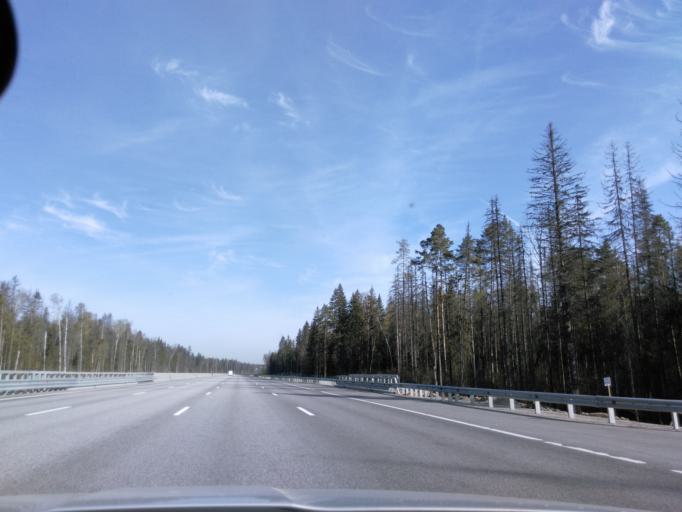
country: RU
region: Moskovskaya
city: Rzhavki
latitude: 56.0181
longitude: 37.2800
